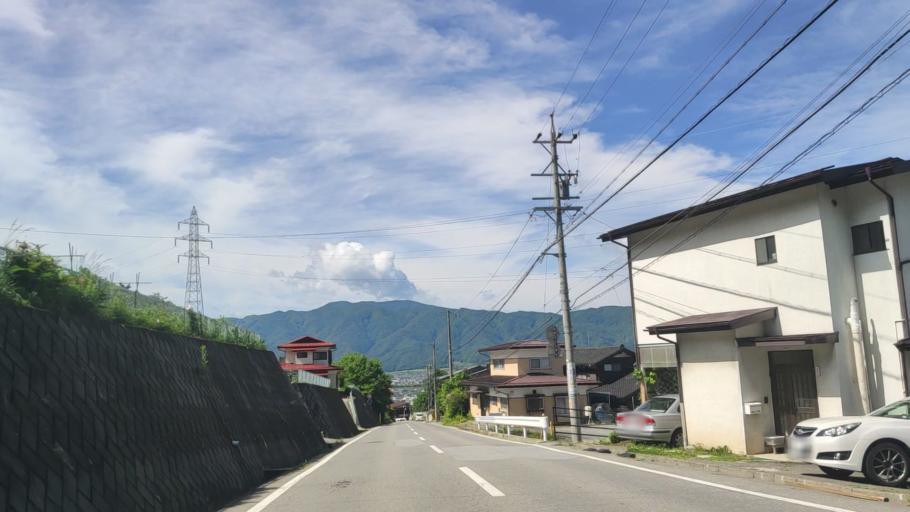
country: JP
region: Nagano
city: Suwa
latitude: 36.0459
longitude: 138.1275
